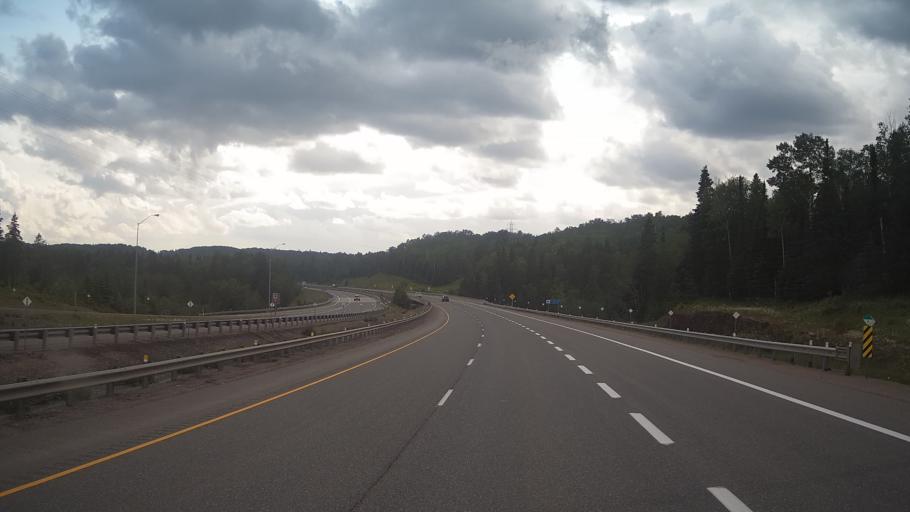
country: CA
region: Ontario
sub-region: Thunder Bay District
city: Thunder Bay
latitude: 48.4835
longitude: -89.1846
